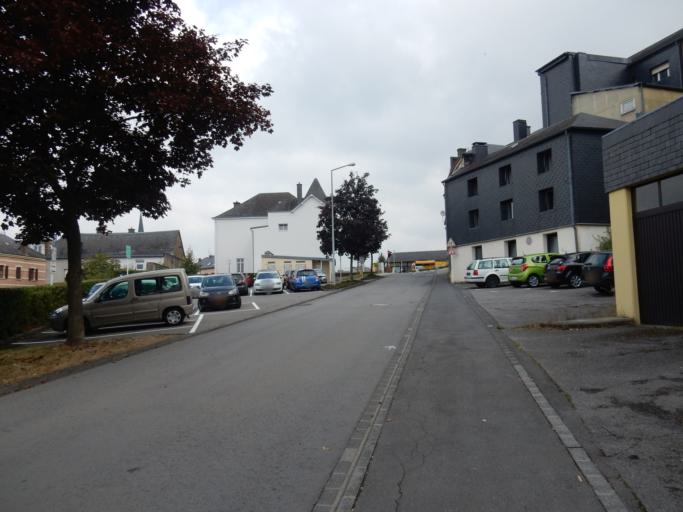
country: LU
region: Diekirch
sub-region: Canton de Wiltz
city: Wiltz
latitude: 49.9678
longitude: 5.9297
